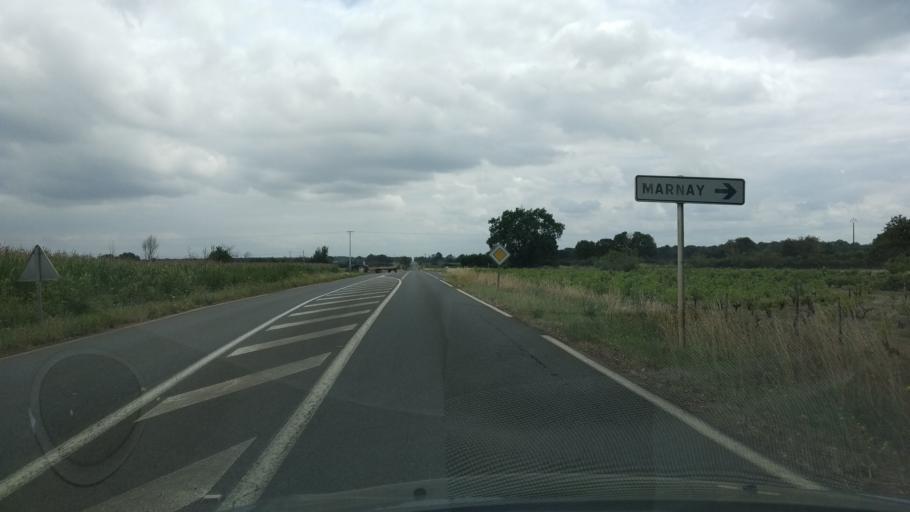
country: FR
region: Poitou-Charentes
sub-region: Departement de la Vienne
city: La Villedieu-du-Clain
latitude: 46.4278
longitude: 0.3780
